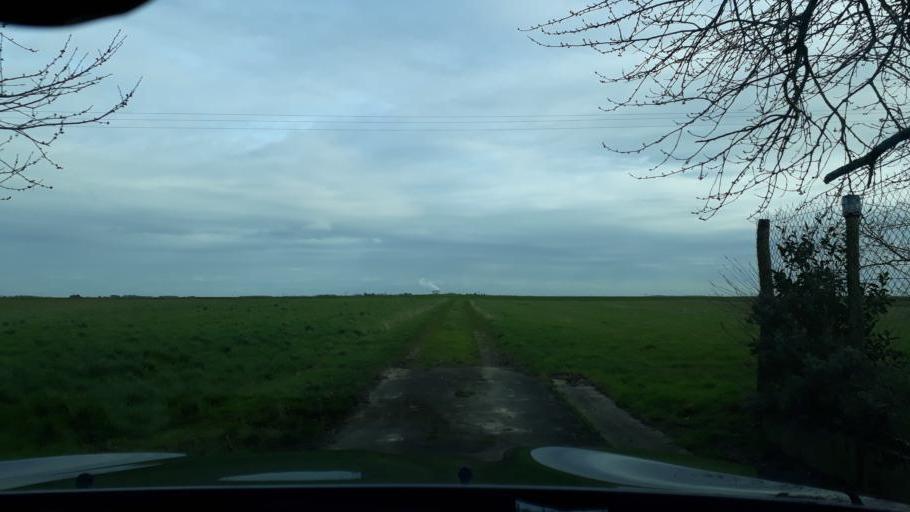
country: FR
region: Centre
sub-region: Departement du Loir-et-Cher
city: Mer
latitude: 47.8000
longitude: 1.4923
